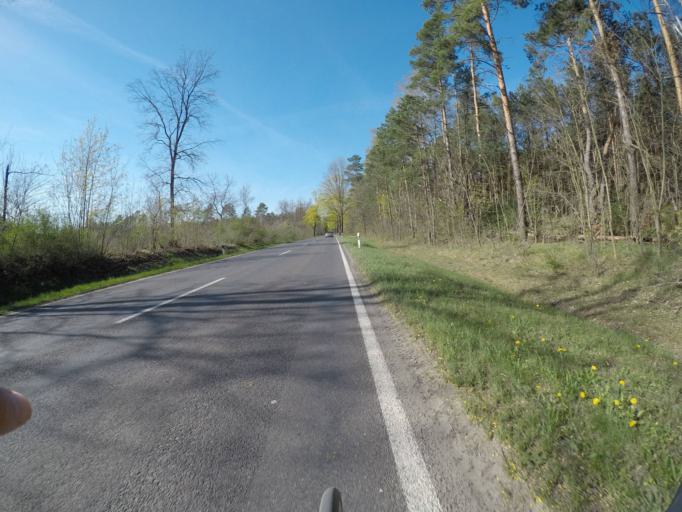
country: DE
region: Brandenburg
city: Grunheide
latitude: 52.4584
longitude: 13.8638
